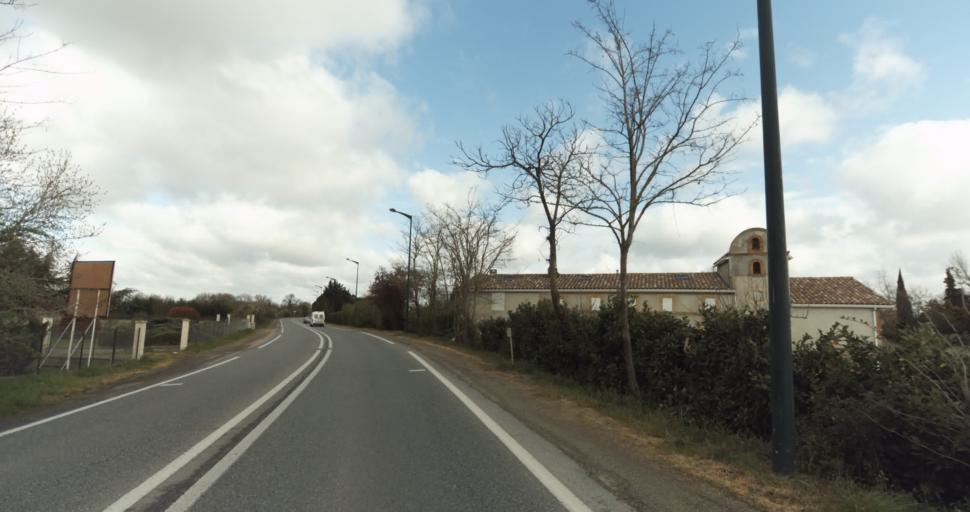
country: FR
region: Midi-Pyrenees
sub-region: Departement de la Haute-Garonne
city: Miremont
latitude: 43.3701
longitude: 1.4492
